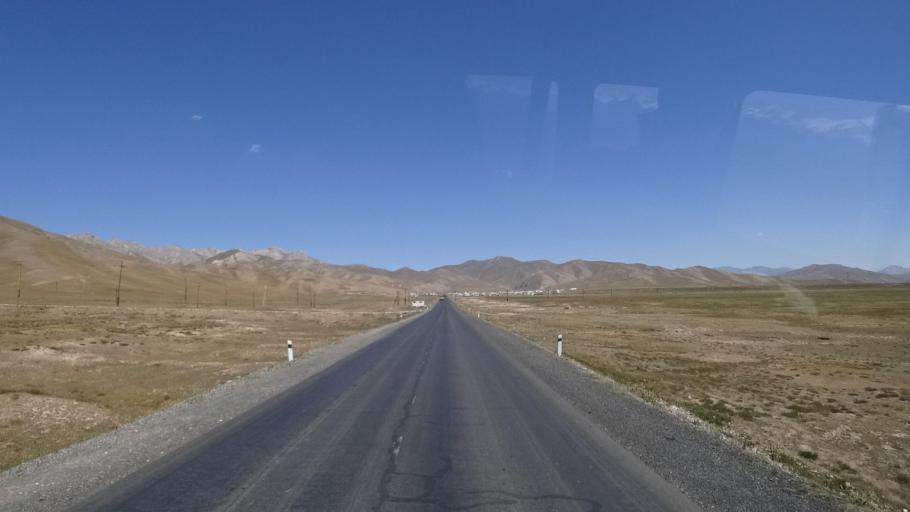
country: KG
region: Osh
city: Gul'cha
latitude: 39.7121
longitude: 73.2362
